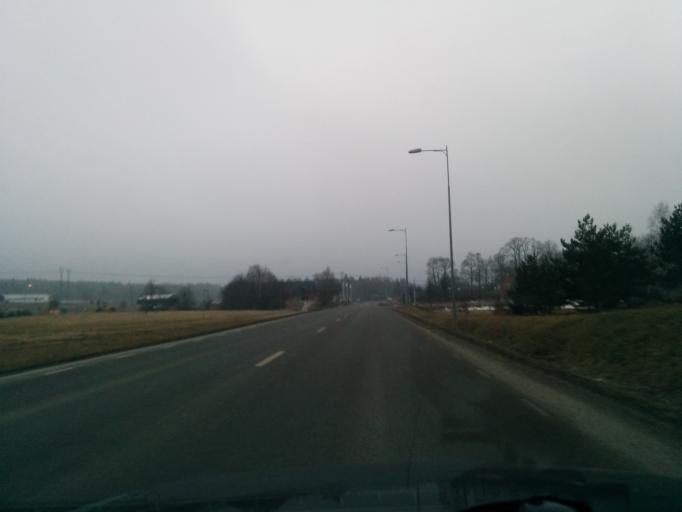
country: SE
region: Stockholm
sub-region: Taby Kommun
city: Taby
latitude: 59.4812
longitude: 18.0541
